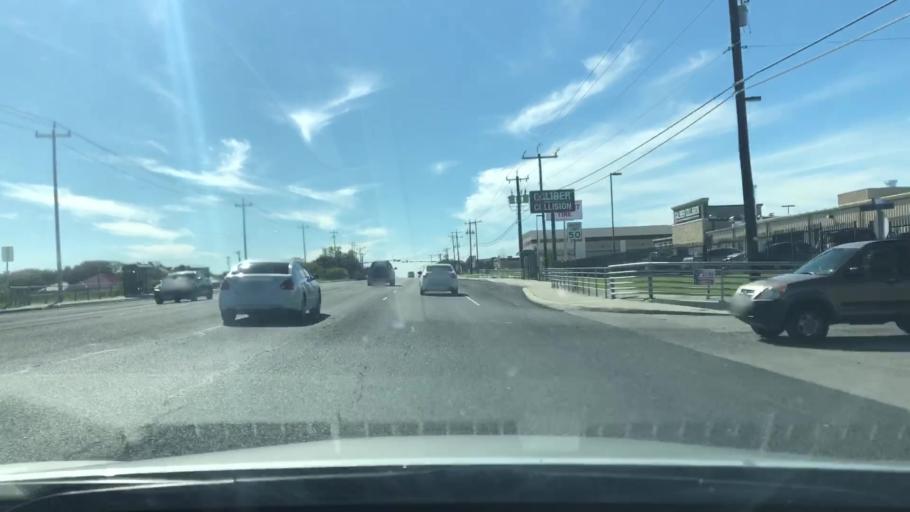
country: US
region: Texas
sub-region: Bexar County
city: Converse
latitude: 29.4909
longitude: -98.3357
